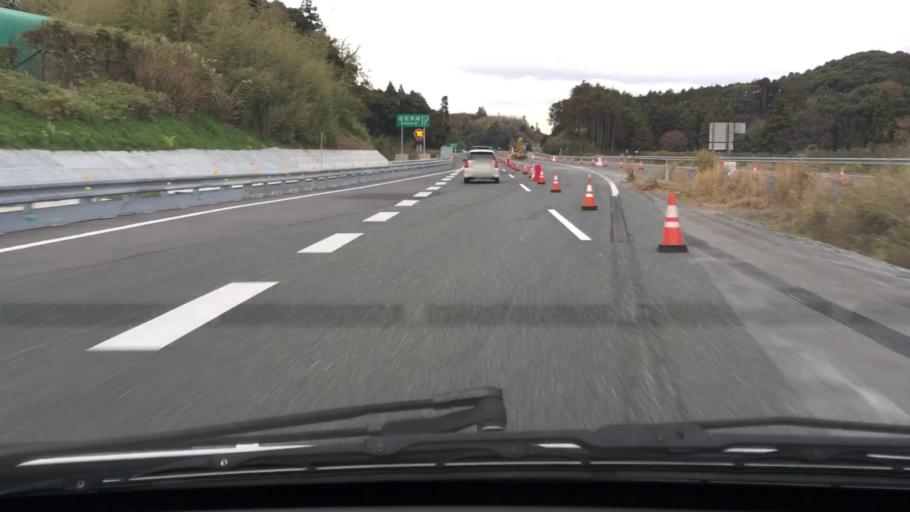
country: JP
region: Chiba
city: Kimitsu
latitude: 35.2855
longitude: 139.9275
